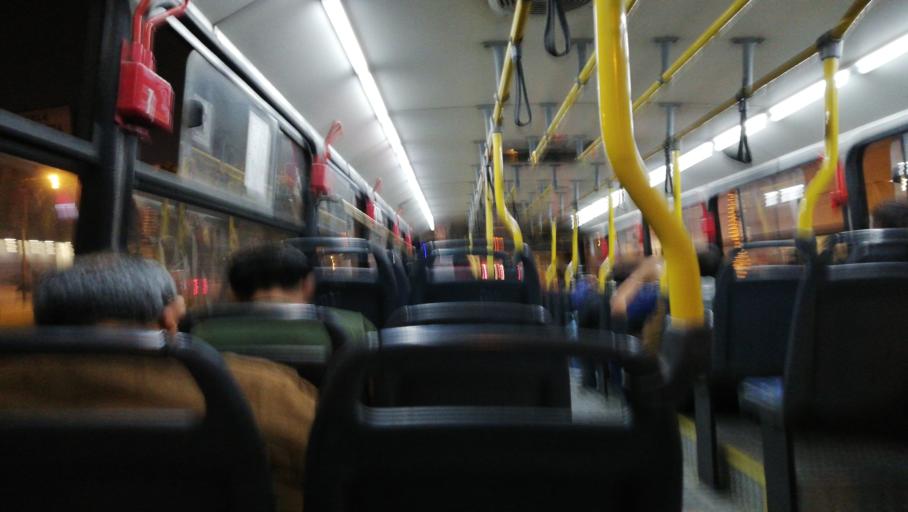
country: PE
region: Lima
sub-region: Lima
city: Surco
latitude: -12.1554
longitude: -76.9826
